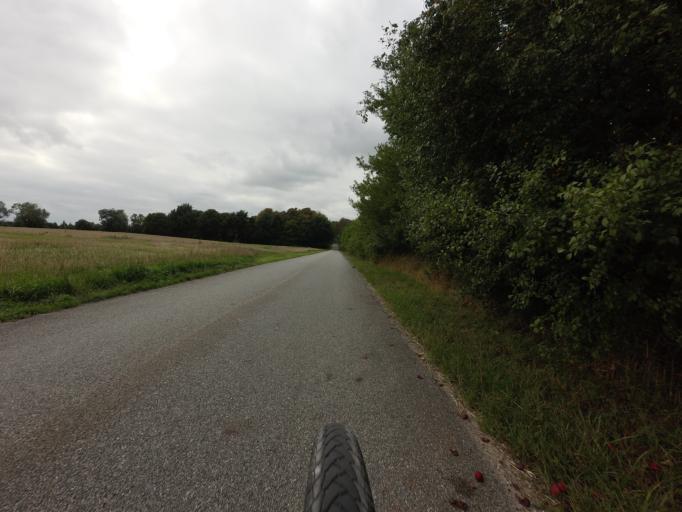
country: DK
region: Zealand
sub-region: Stevns Kommune
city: Store Heddinge
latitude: 55.3391
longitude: 12.4263
